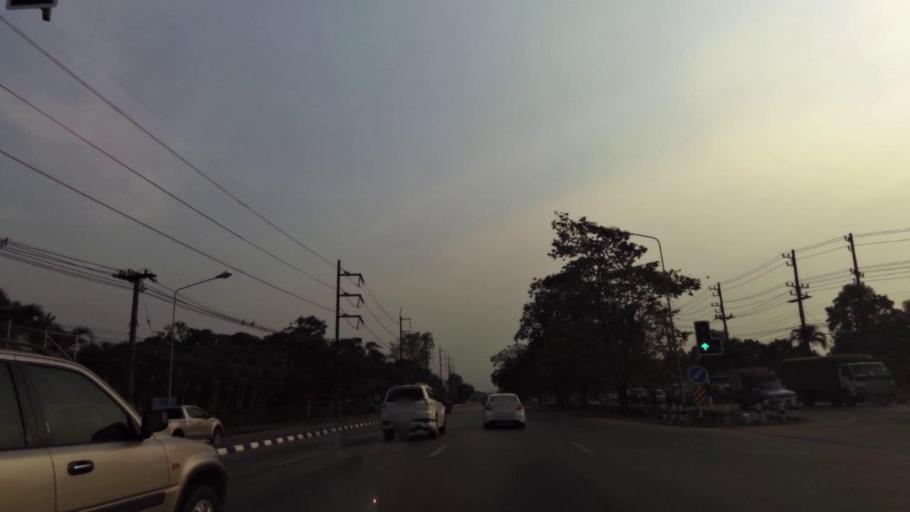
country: TH
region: Chanthaburi
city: Khlung
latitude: 12.5108
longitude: 102.1691
